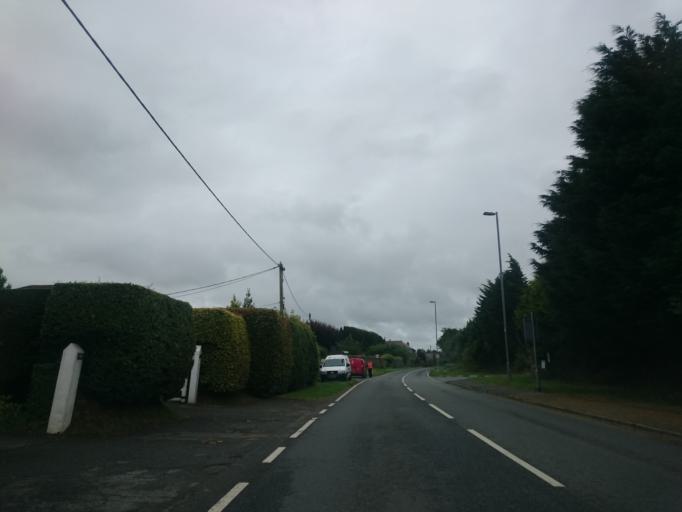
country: GB
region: Wales
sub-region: Pembrokeshire
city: Haverfordwest
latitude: 51.7846
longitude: -4.9735
